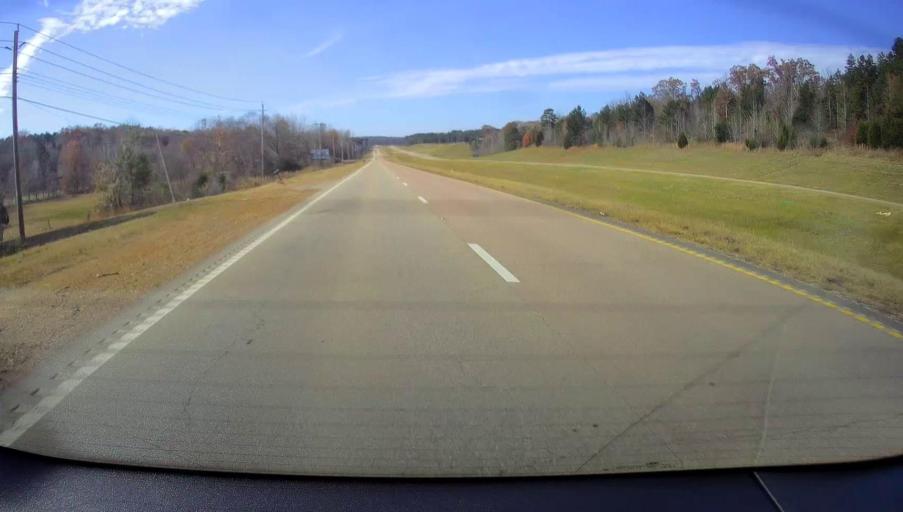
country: US
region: Mississippi
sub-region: Tippah County
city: Ripley
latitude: 34.9503
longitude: -88.9234
